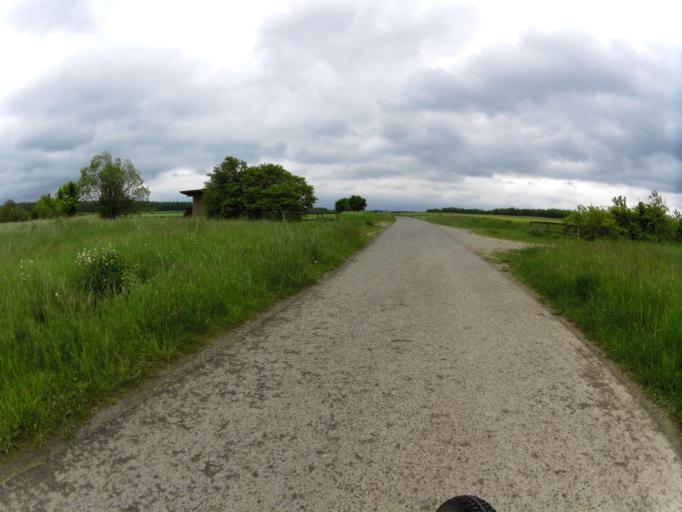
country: DE
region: Bavaria
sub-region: Regierungsbezirk Unterfranken
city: Volkach
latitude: 49.8568
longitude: 10.2419
